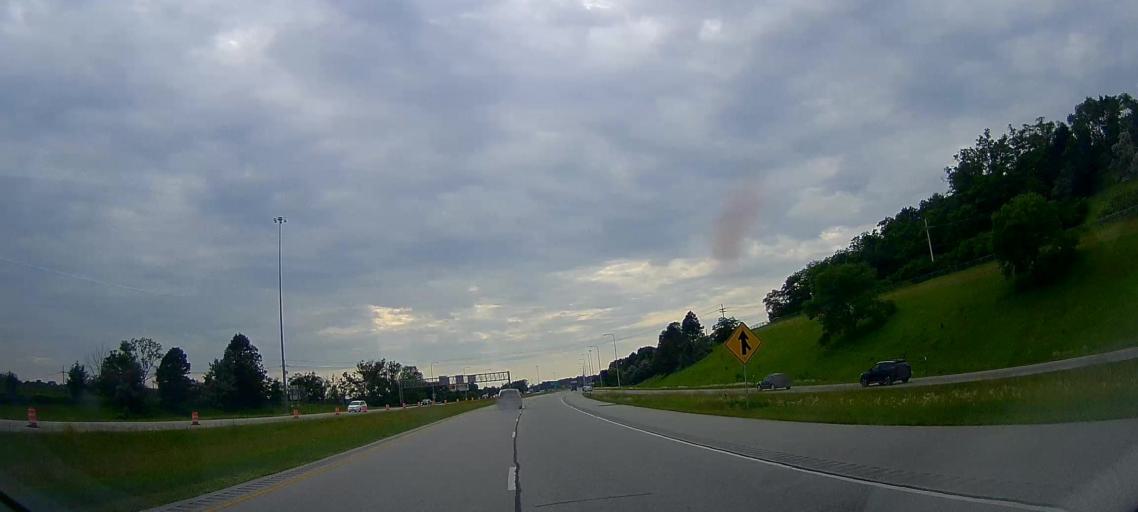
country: US
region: Iowa
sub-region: Pottawattamie County
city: Carter Lake
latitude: 41.3448
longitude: -95.9678
